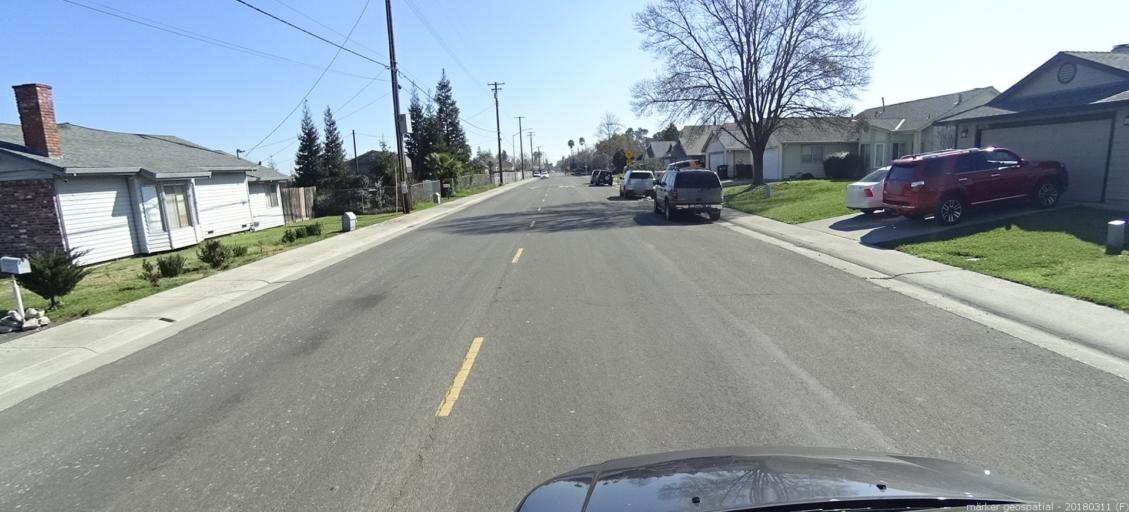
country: US
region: California
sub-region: Sacramento County
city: Florin
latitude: 38.4653
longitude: -121.4040
